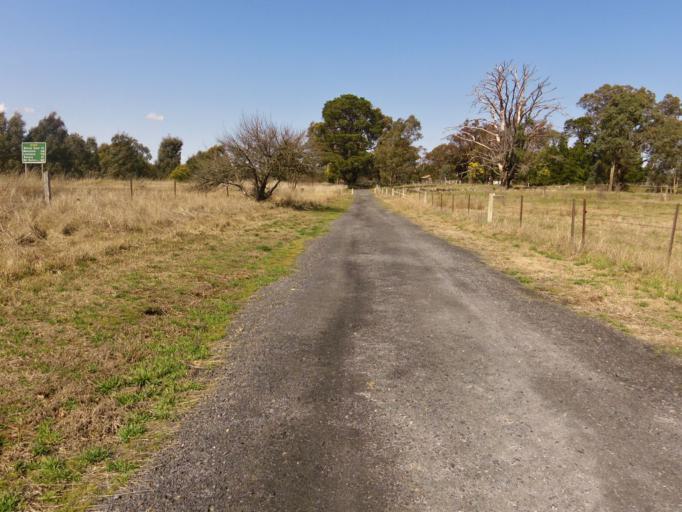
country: AU
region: Victoria
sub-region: Murrindindi
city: Alexandra
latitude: -36.9794
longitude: 145.7159
